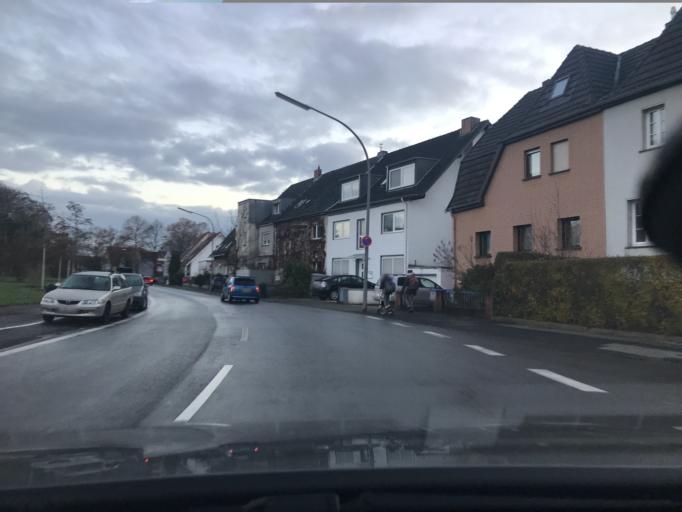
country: DE
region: North Rhine-Westphalia
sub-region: Regierungsbezirk Koln
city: Merheim
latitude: 50.9692
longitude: 7.0664
